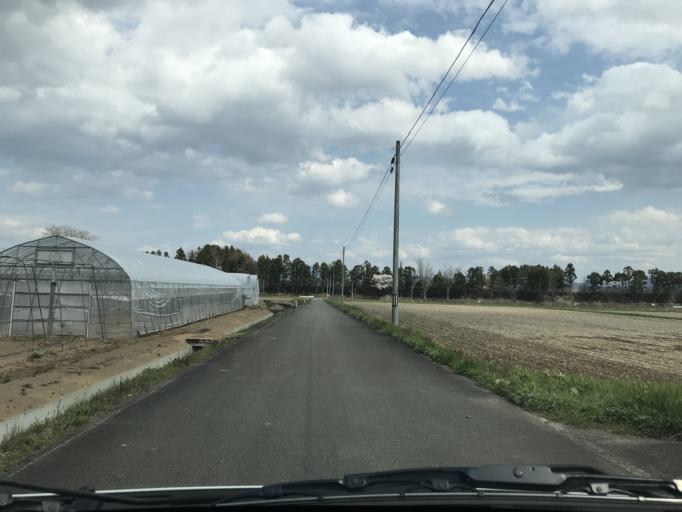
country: JP
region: Iwate
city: Mizusawa
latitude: 39.0803
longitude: 141.0991
